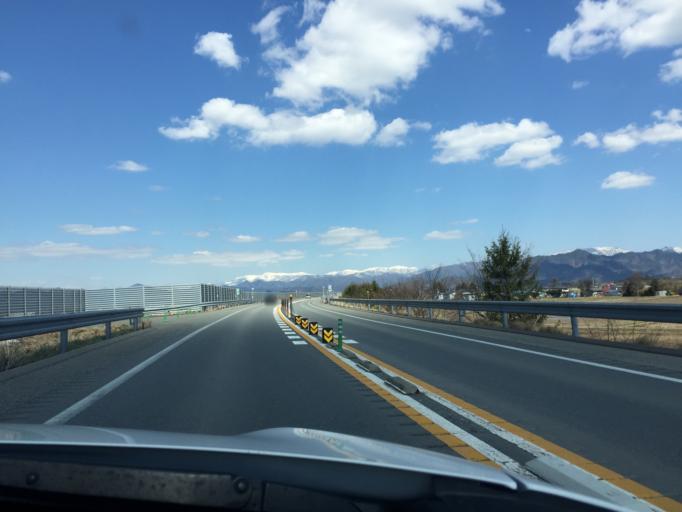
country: JP
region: Yamagata
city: Yonezawa
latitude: 37.9689
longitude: 140.1253
